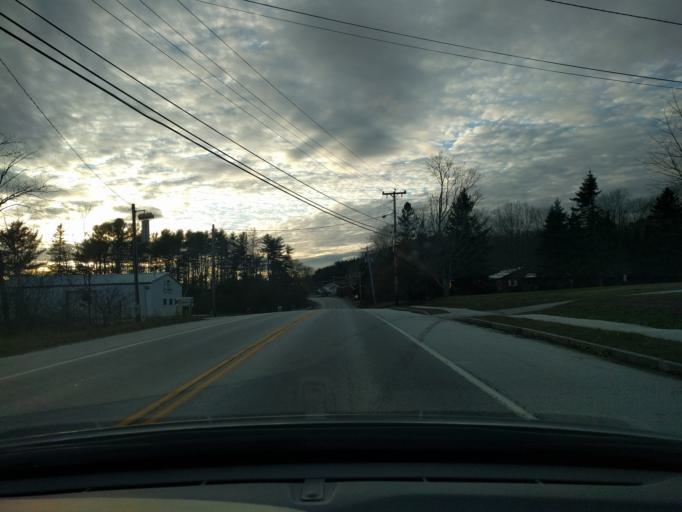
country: US
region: Maine
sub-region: Waldo County
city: Winterport
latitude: 44.6304
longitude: -68.8586
